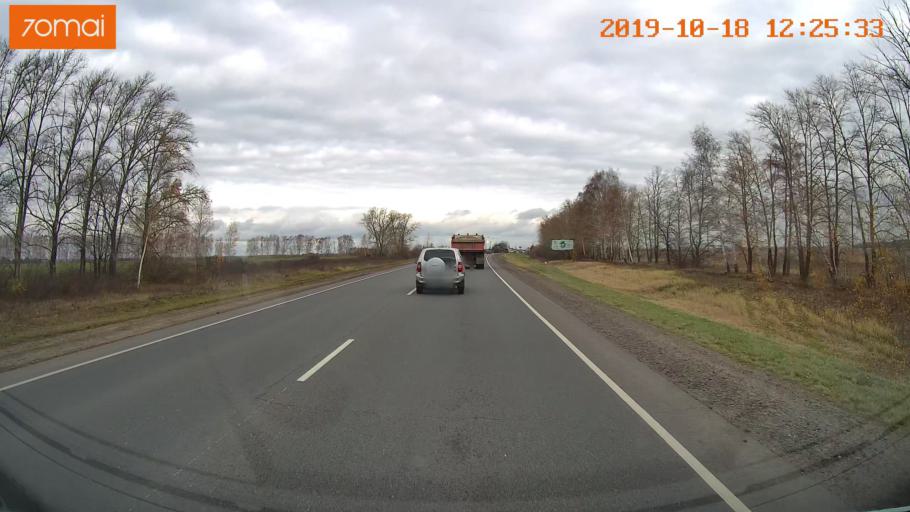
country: RU
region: Rjazan
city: Rybnoye
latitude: 54.5511
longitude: 39.5219
